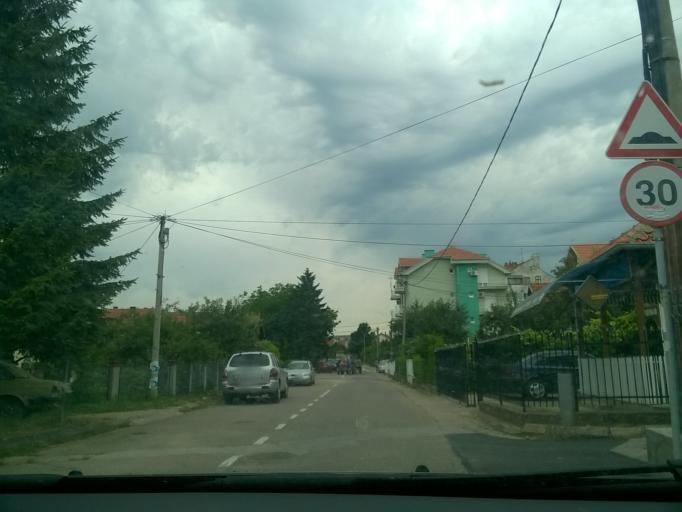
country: RS
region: Central Serbia
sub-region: Zajecarski Okrug
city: Soko Banja
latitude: 43.6490
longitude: 21.8789
